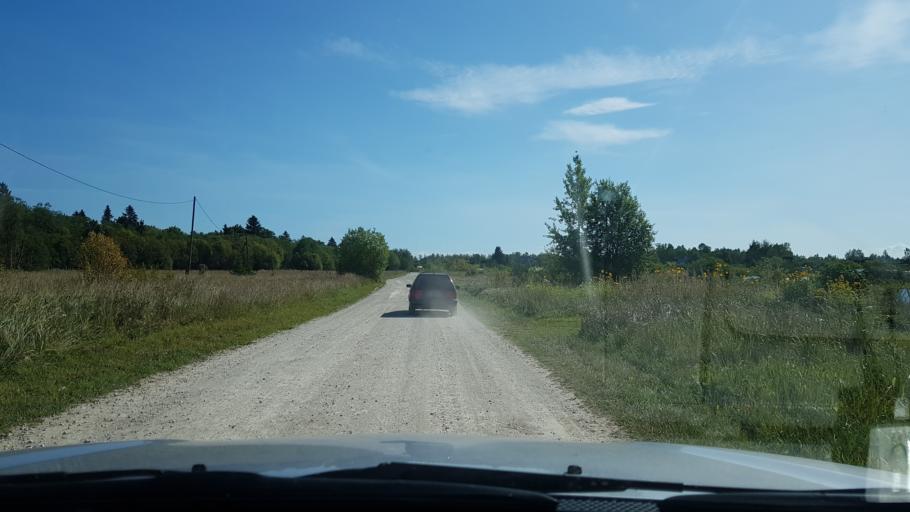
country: EE
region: Ida-Virumaa
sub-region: Sillamaee linn
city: Sillamae
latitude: 59.3741
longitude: 27.7841
